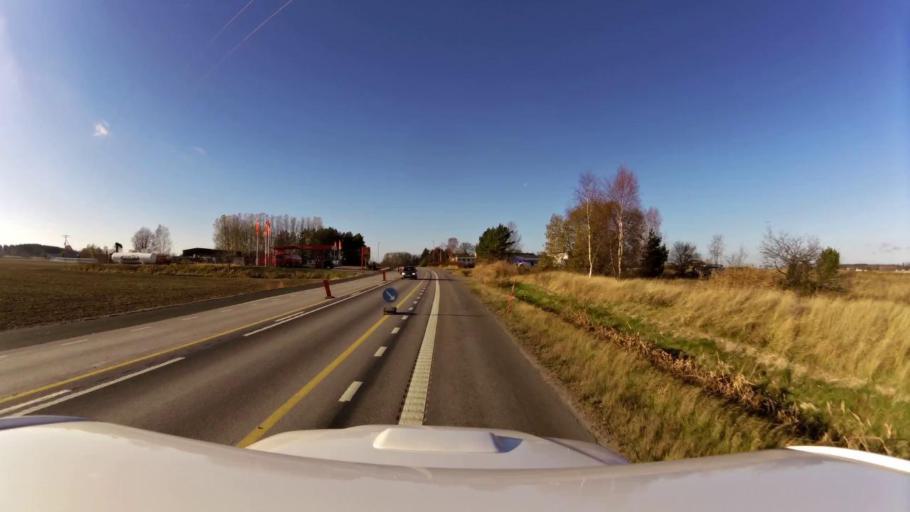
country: SE
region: OEstergoetland
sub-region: Linkopings Kommun
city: Linghem
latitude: 58.4380
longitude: 15.7530
